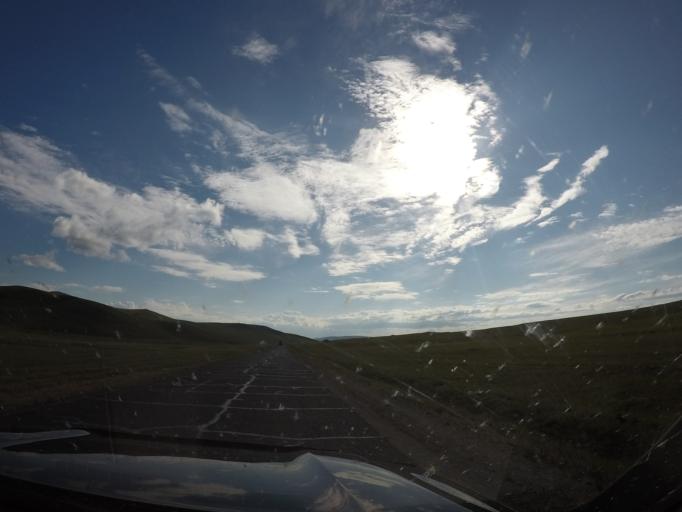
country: MN
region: Hentiy
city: Modot
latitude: 47.8000
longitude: 108.6980
